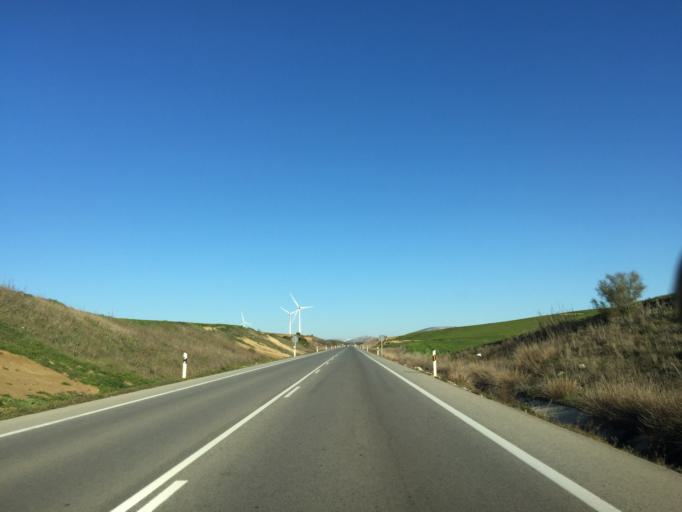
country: ES
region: Andalusia
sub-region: Provincia de Malaga
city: Ardales
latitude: 36.9243
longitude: -4.8477
